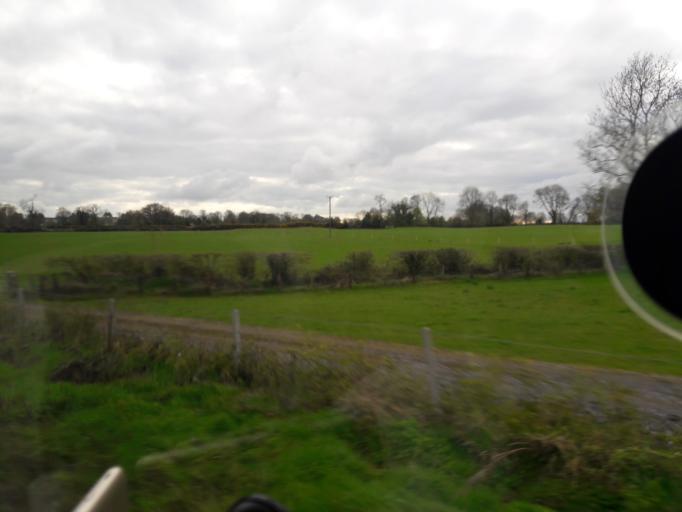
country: IE
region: Leinster
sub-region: An Iarmhi
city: An Muileann gCearr
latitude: 53.6207
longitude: -7.4141
